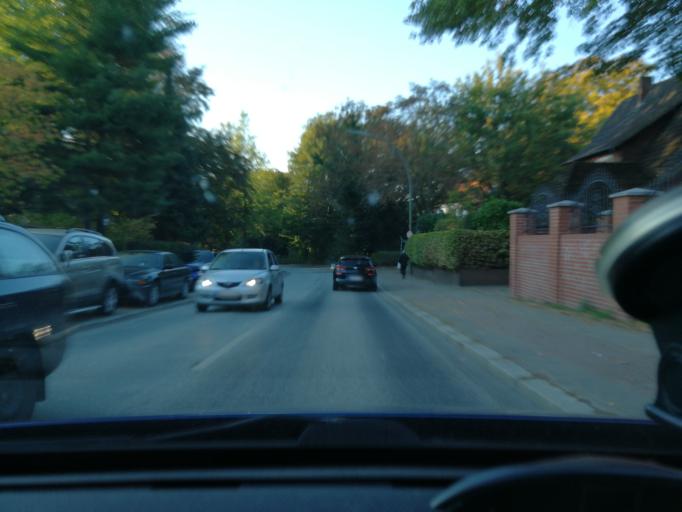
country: DE
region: Hamburg
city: Harburg
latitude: 53.4642
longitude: 9.9561
